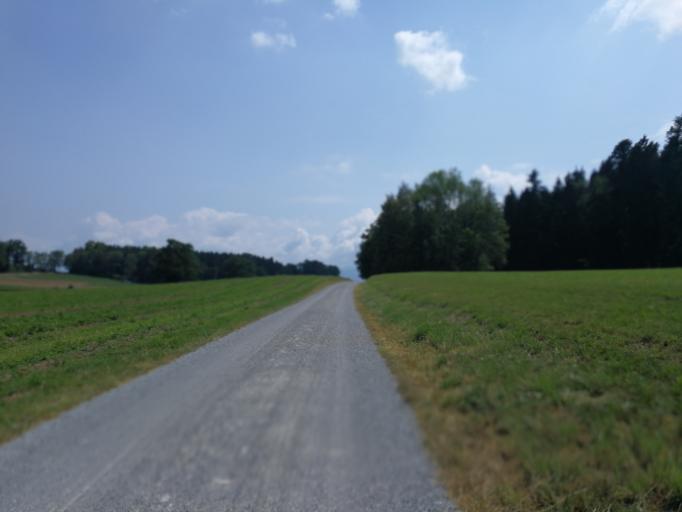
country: CH
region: Zurich
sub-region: Bezirk Hinwil
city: Binzikon
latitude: 47.2723
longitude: 8.7560
